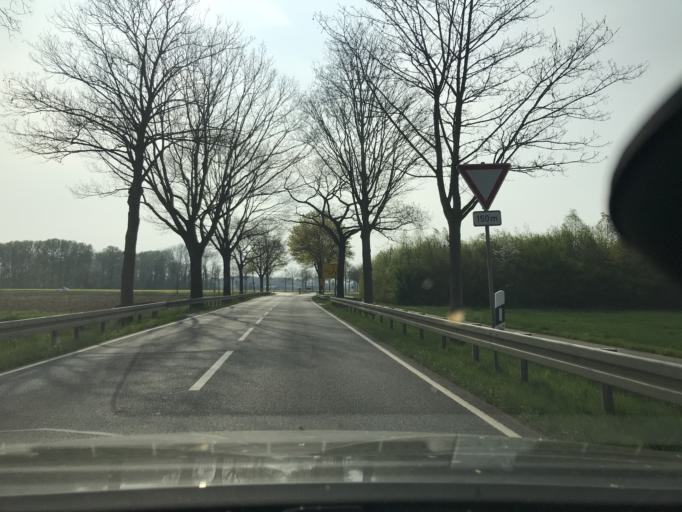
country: DE
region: North Rhine-Westphalia
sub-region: Regierungsbezirk Dusseldorf
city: Wachtendonk
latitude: 51.4542
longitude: 6.3325
